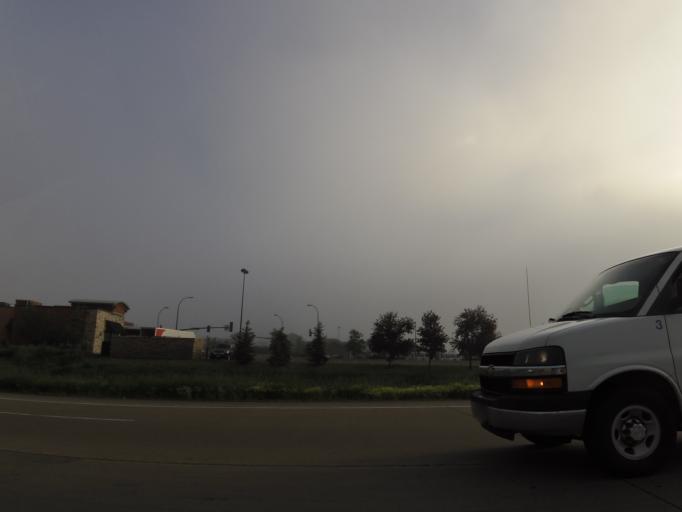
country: US
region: Minnesota
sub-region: Hennepin County
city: Maple Grove
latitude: 45.0900
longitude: -93.4335
